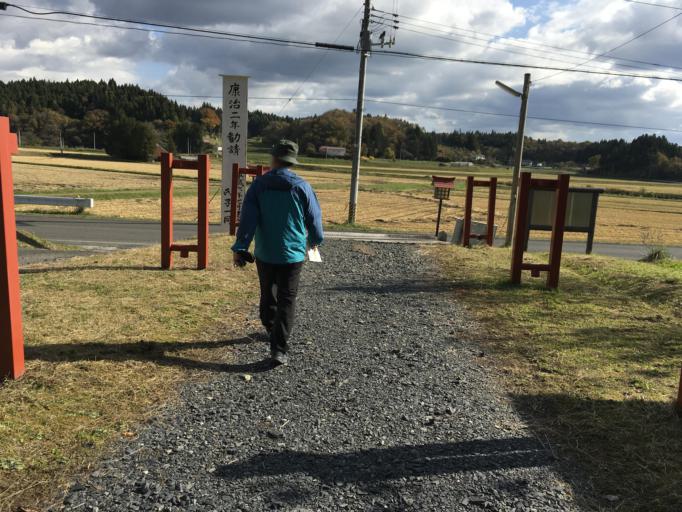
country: JP
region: Iwate
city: Ichinoseki
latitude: 38.9531
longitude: 141.3519
